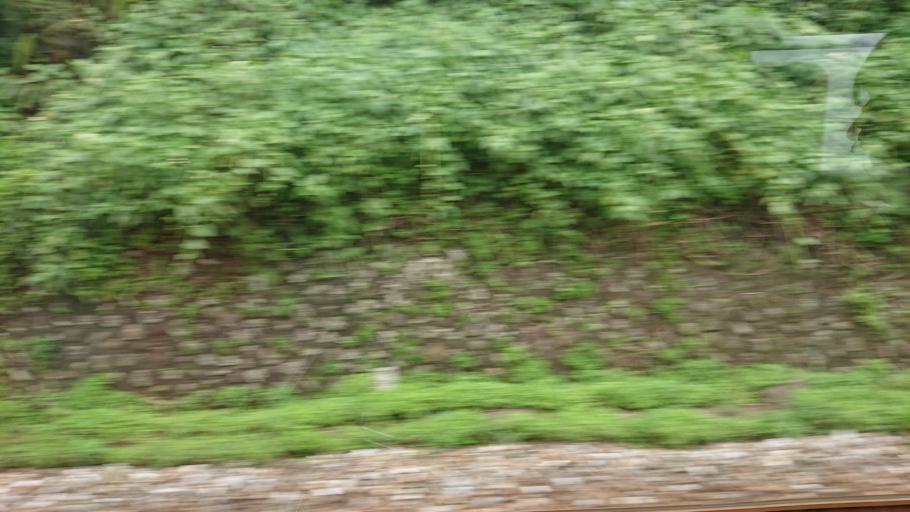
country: TW
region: Taiwan
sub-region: Yilan
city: Yilan
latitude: 24.9080
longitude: 121.8730
